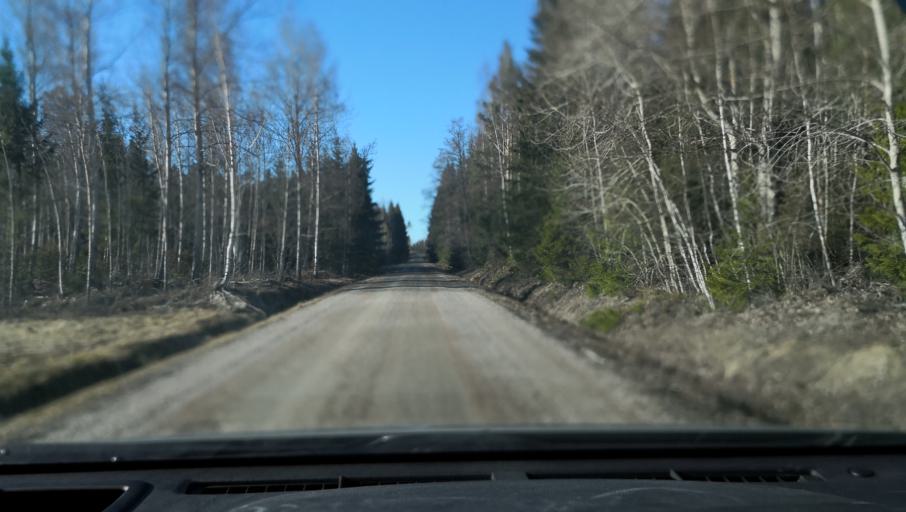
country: SE
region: Vaestmanland
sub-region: Sala Kommun
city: Sala
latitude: 60.1554
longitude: 16.6315
